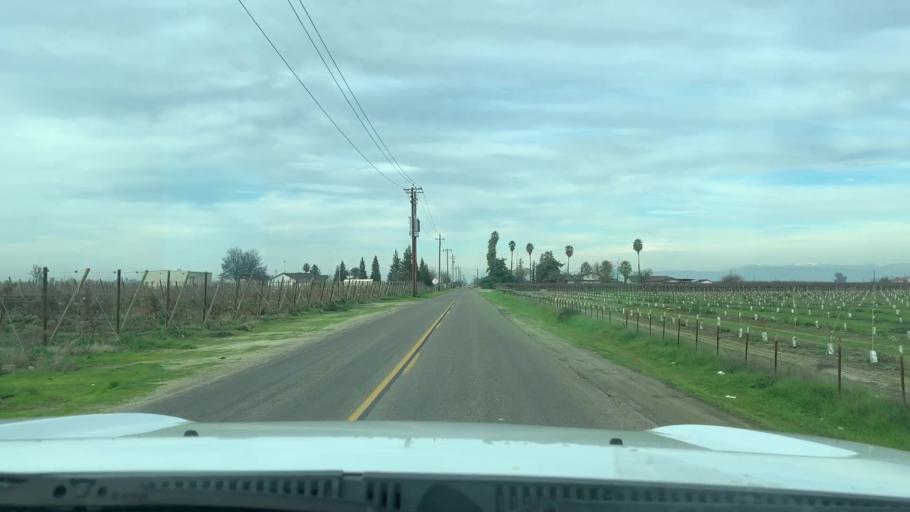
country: US
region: California
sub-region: Fresno County
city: Selma
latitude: 36.5617
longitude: -119.5750
